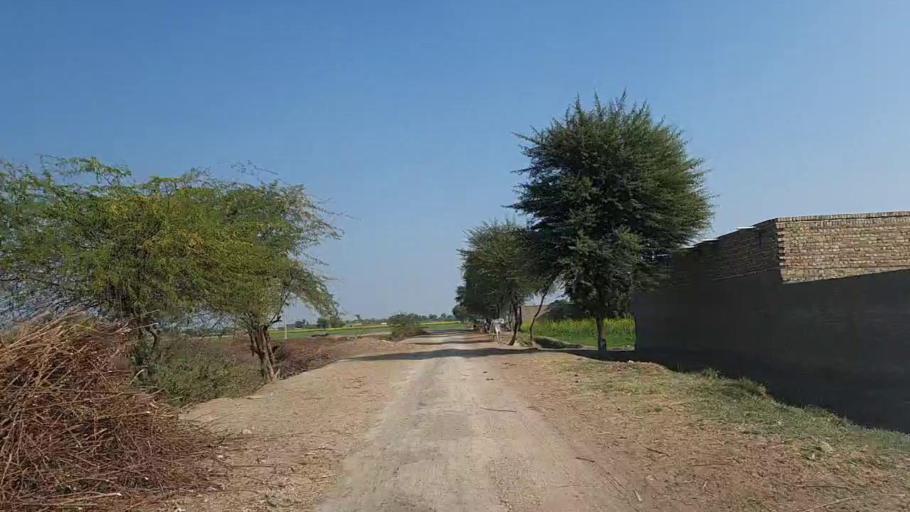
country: PK
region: Sindh
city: Jam Sahib
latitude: 26.2540
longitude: 68.5709
